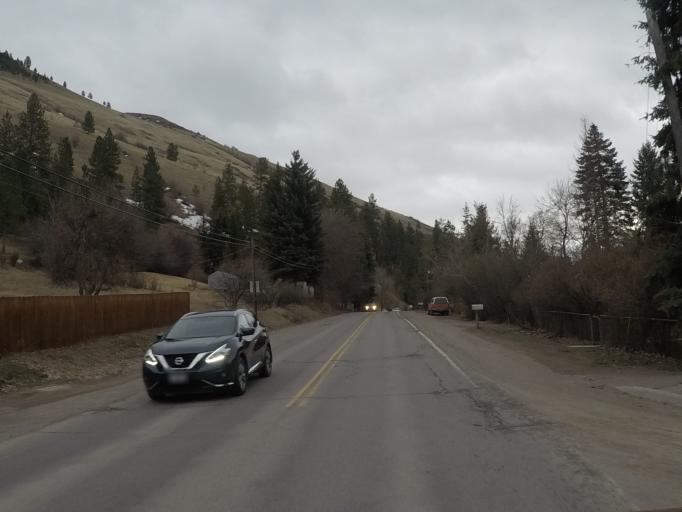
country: US
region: Montana
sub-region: Missoula County
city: Missoula
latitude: 46.8802
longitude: -113.9698
